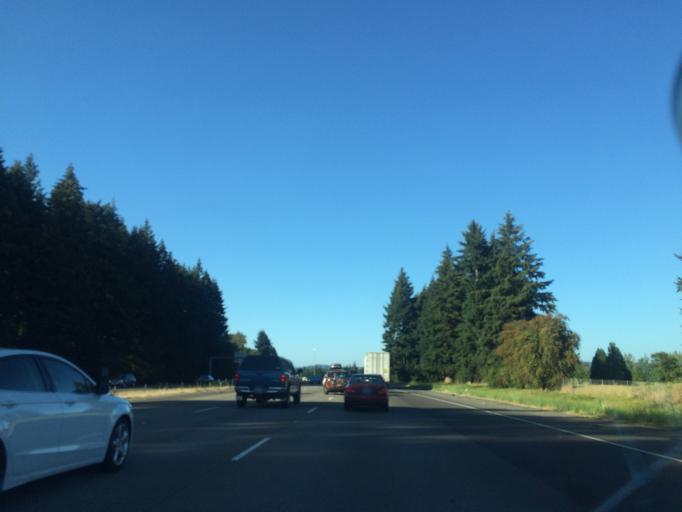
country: US
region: Oregon
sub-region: Clackamas County
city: Wilsonville
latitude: 45.2752
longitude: -122.7732
